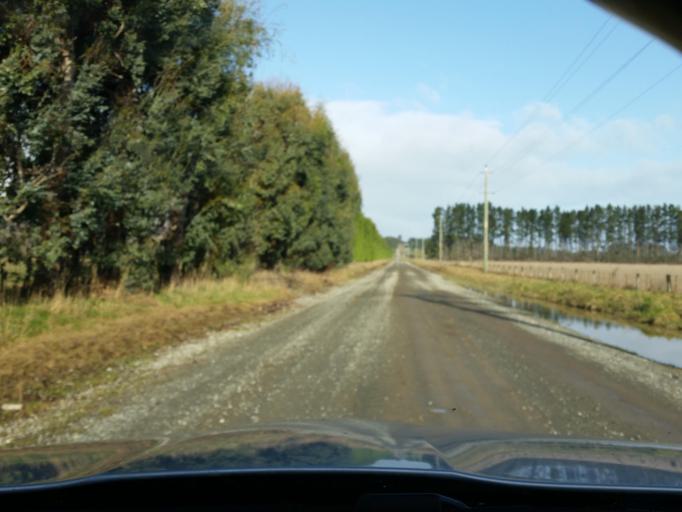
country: NZ
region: Southland
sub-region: Southland District
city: Te Anau
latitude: -45.5565
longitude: 167.7057
